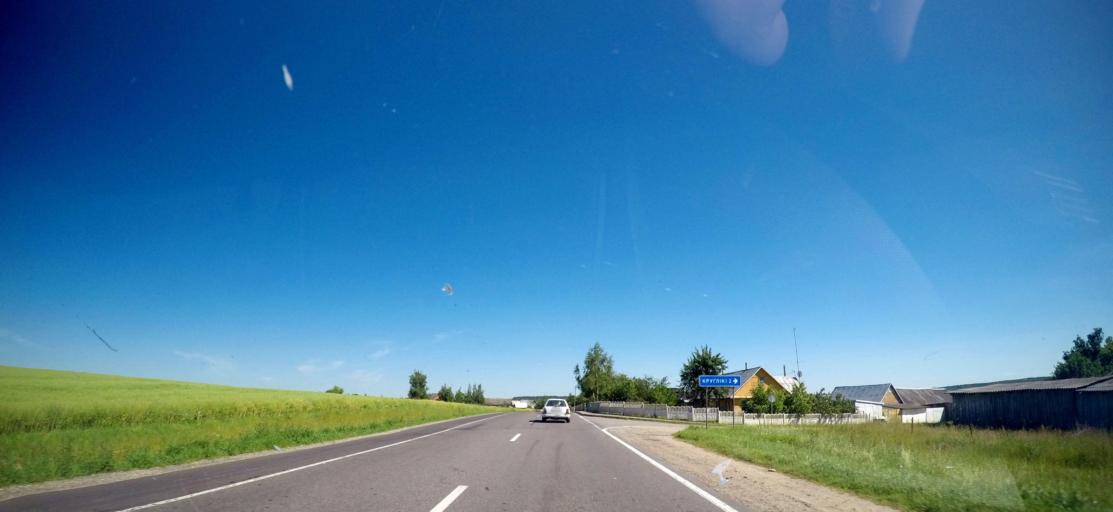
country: BY
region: Grodnenskaya
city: Indura
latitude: 53.4476
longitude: 23.9092
